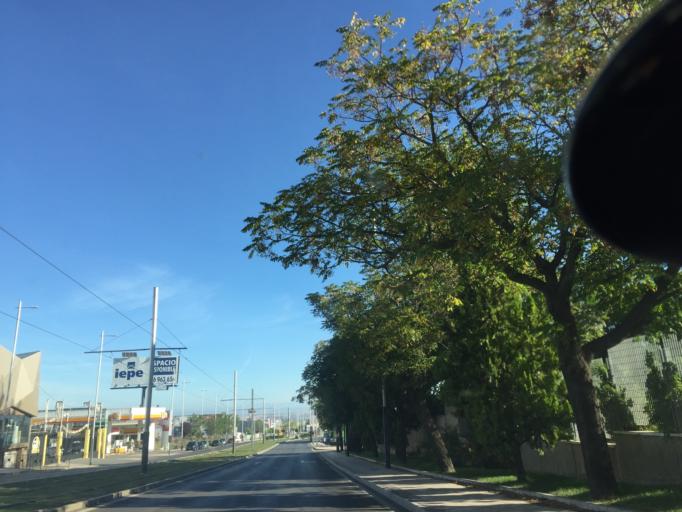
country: ES
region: Andalusia
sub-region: Provincia de Jaen
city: Jaen
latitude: 37.7874
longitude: -3.7826
